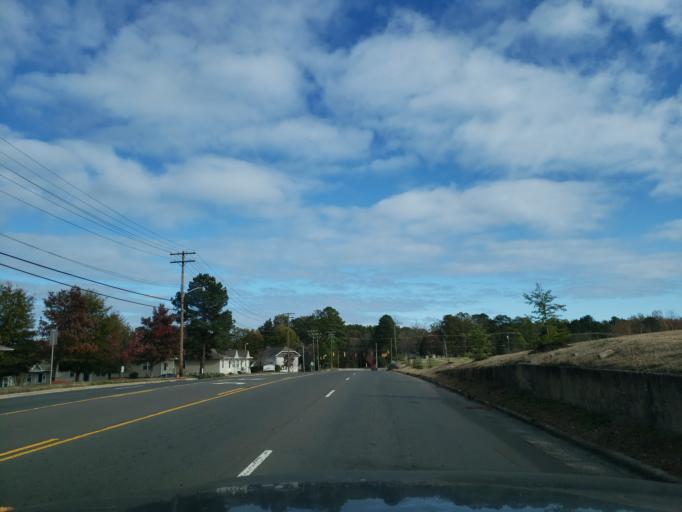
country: US
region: North Carolina
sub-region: Durham County
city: Durham
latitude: 35.9603
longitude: -78.9127
